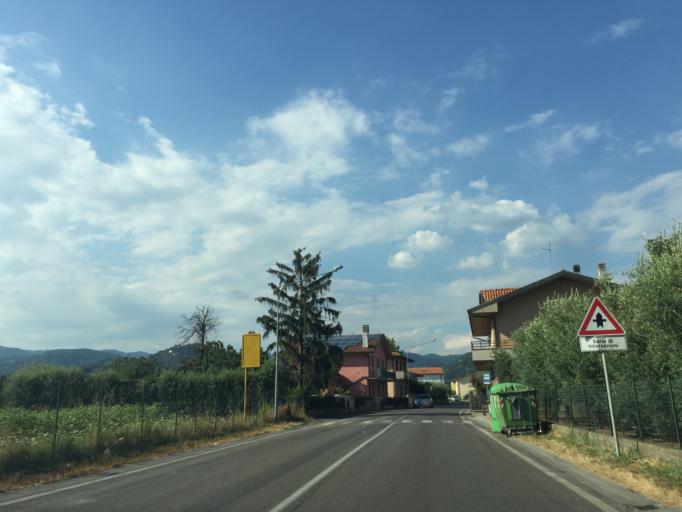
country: IT
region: Tuscany
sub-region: Provincia di Pistoia
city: Pieve a Nievole
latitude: 43.8685
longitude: 10.7982
